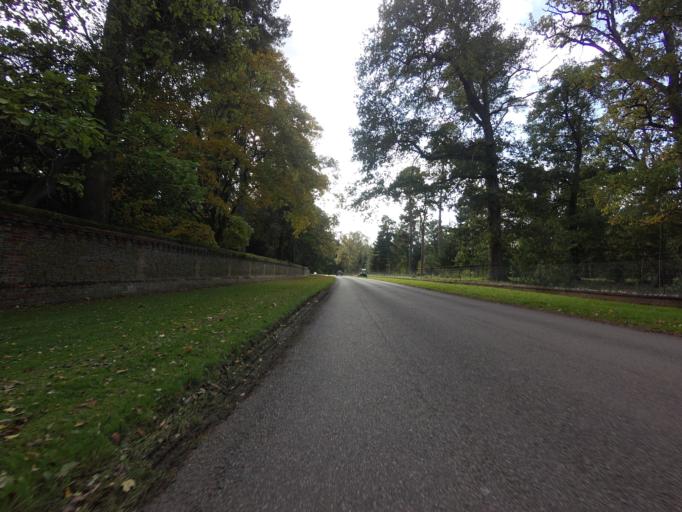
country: GB
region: England
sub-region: Norfolk
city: Dersingham
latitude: 52.8325
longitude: 0.5119
